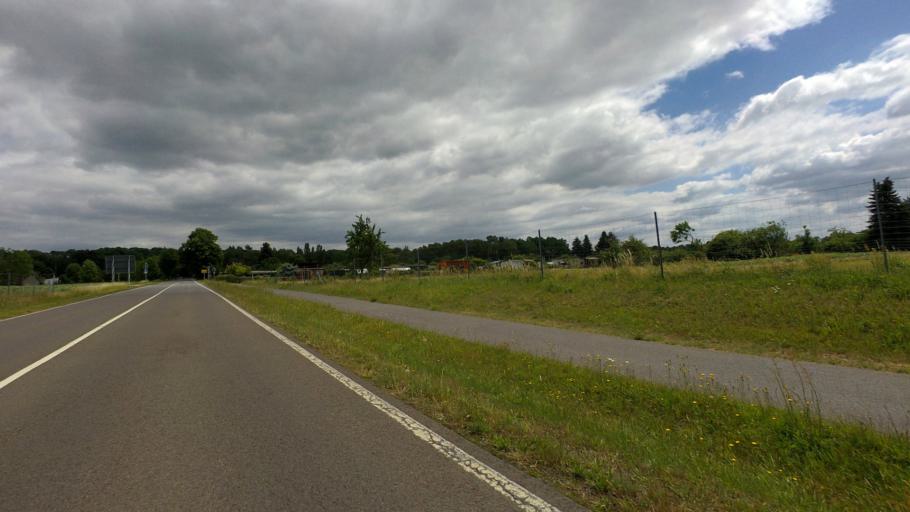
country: DE
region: Brandenburg
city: Luckau
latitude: 51.8533
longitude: 13.6880
